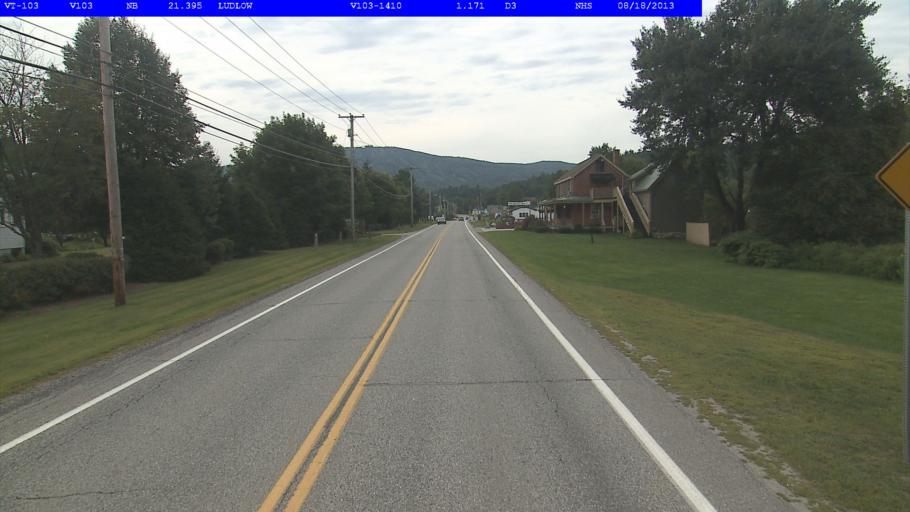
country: US
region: Vermont
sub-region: Windsor County
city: Chester
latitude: 43.3947
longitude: -72.6823
